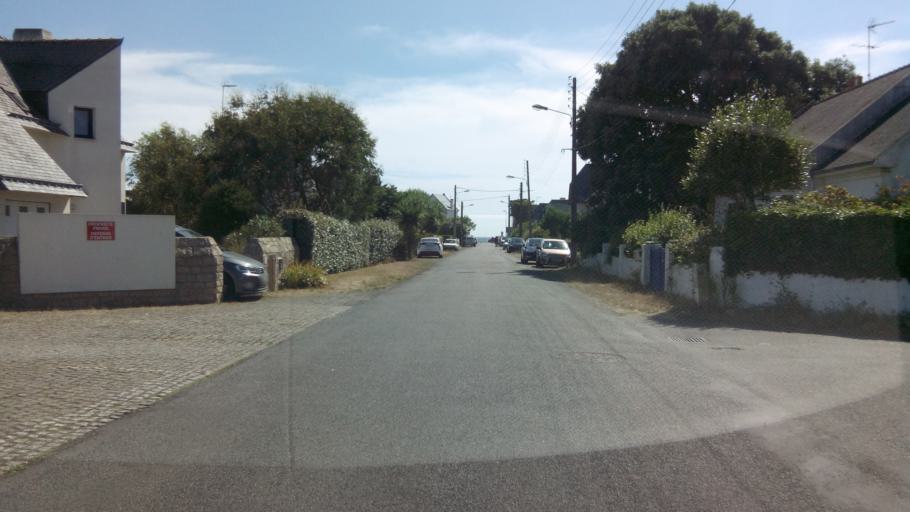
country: FR
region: Pays de la Loire
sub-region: Departement de la Loire-Atlantique
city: Le Croisic
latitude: 47.2847
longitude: -2.5094
